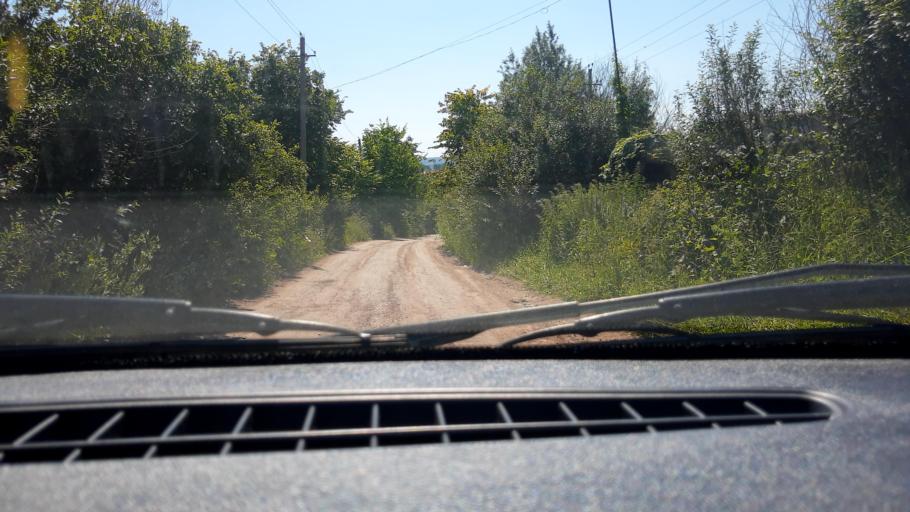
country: RU
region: Bashkortostan
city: Karmaskaly
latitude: 54.3622
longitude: 55.8938
